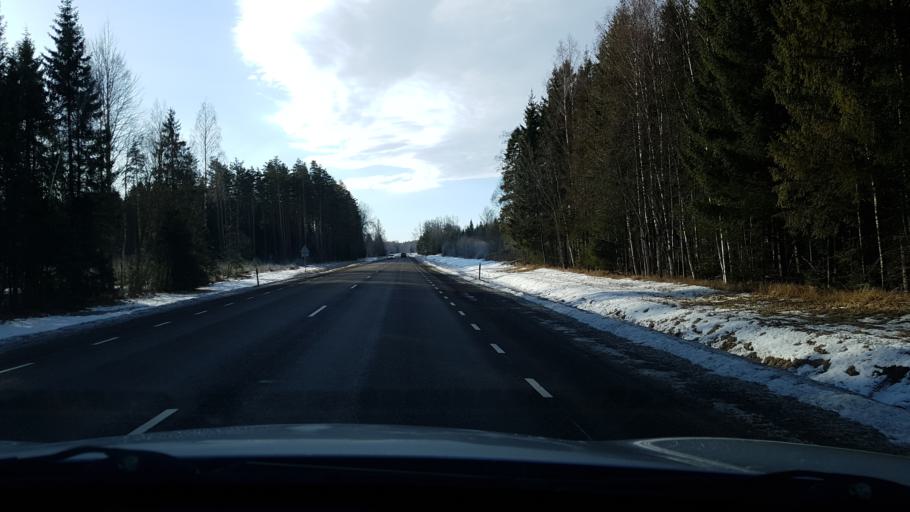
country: EE
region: Viljandimaa
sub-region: Vohma linn
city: Vohma
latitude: 58.5934
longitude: 25.5719
